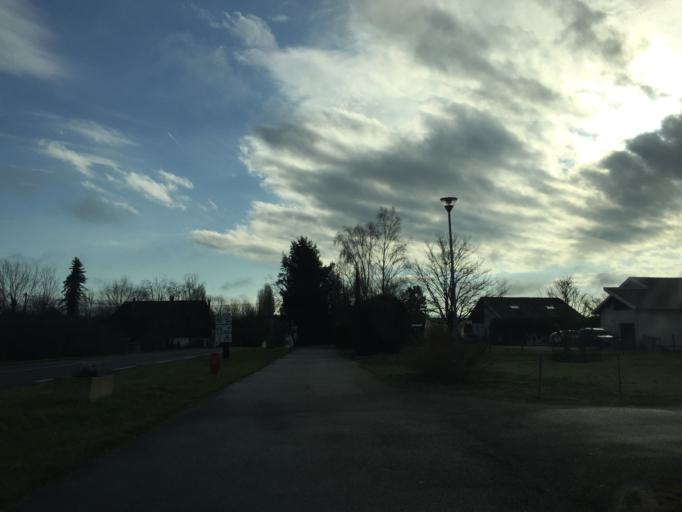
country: FR
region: Franche-Comte
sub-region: Departement du Jura
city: Mont-sous-Vaudrey
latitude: 46.9768
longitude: 5.6148
